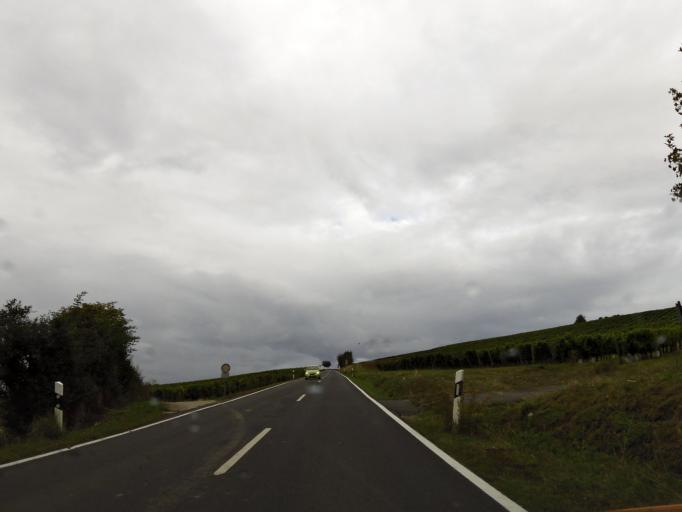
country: DE
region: Rheinland-Pfalz
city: Volxheim
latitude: 49.8137
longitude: 7.9401
